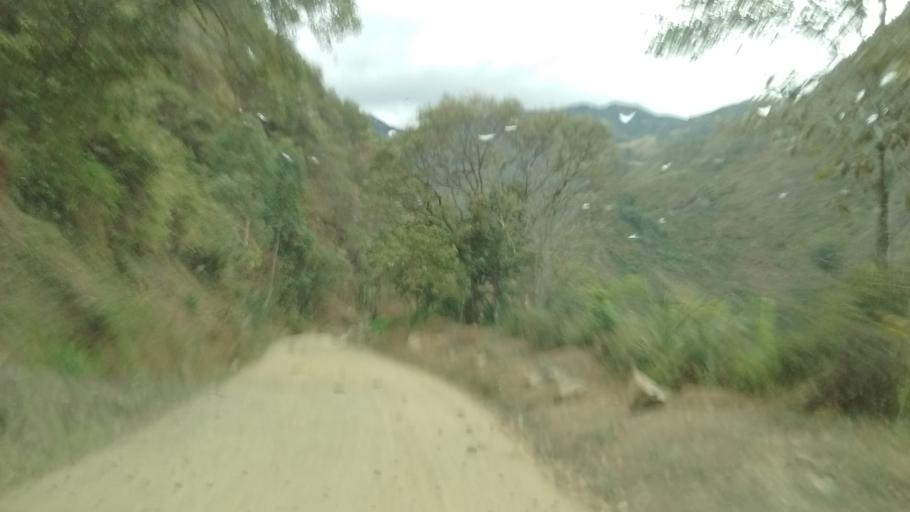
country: CO
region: Cauca
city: La Vega
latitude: 2.0385
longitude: -76.7973
